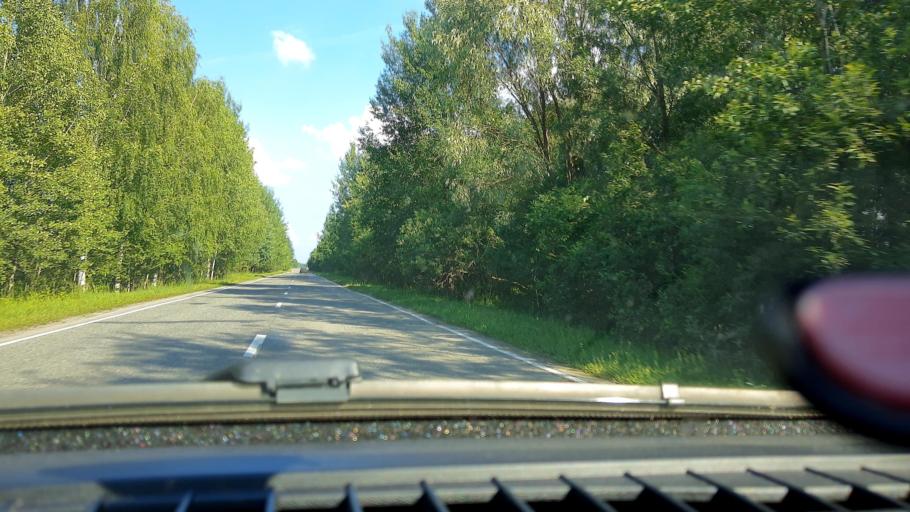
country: RU
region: Nizjnij Novgorod
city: Neklyudovo
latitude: 56.5094
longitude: 43.9610
